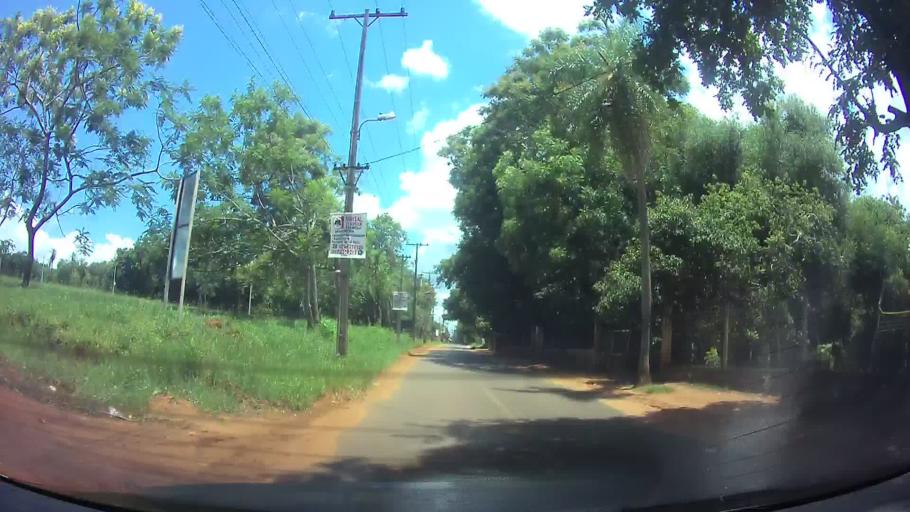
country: PY
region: Central
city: Itaugua
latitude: -25.3755
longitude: -57.3662
